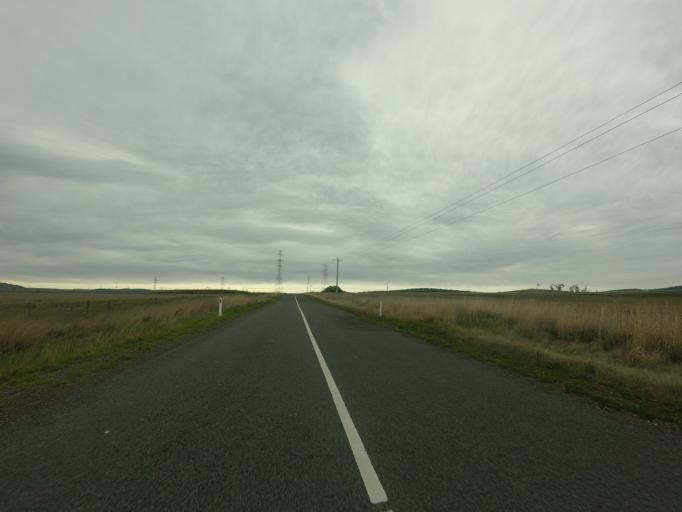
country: AU
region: Tasmania
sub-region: Derwent Valley
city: New Norfolk
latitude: -42.4207
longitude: 147.0017
